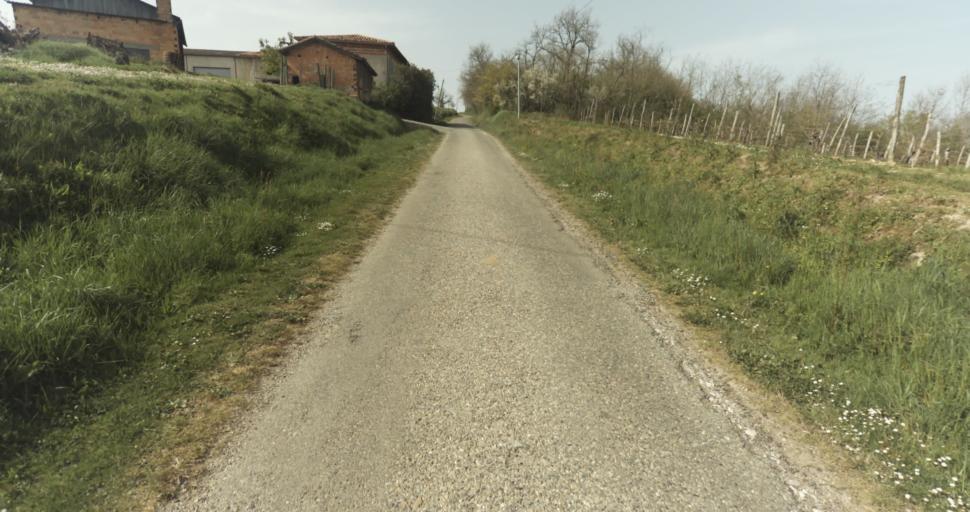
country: FR
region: Midi-Pyrenees
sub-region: Departement du Tarn-et-Garonne
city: Moissac
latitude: 44.1379
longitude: 1.1535
